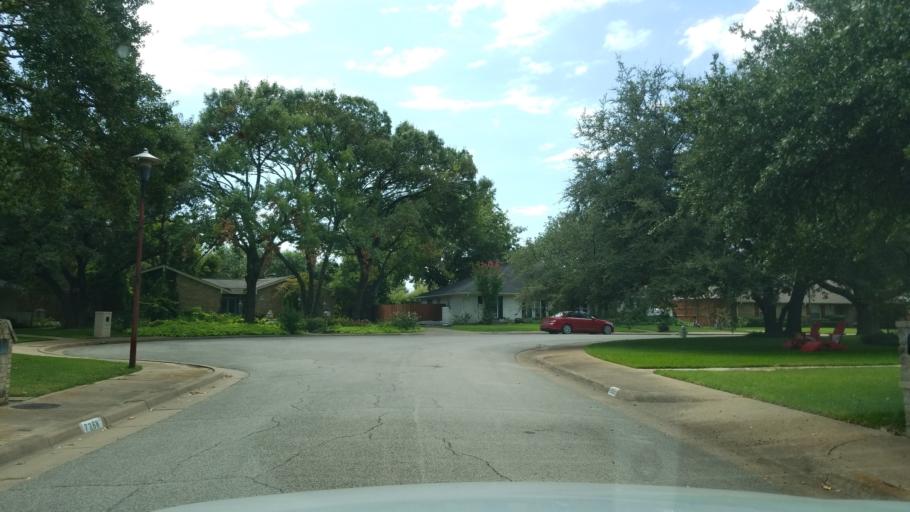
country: US
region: Texas
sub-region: Dallas County
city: Addison
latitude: 32.9510
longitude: -96.7804
